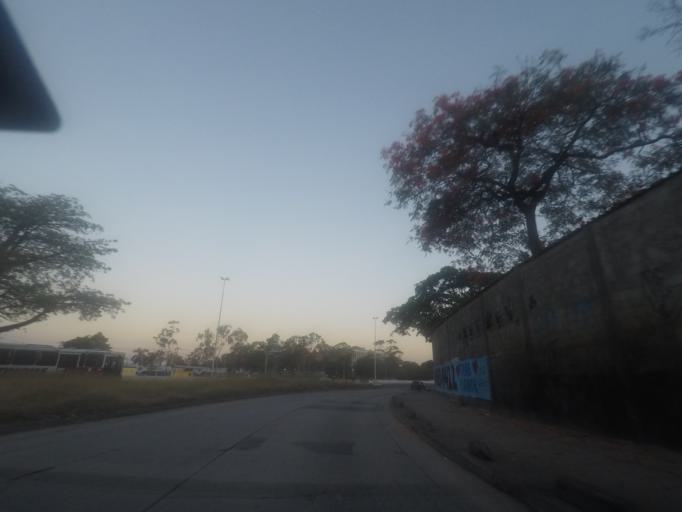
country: BR
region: Rio de Janeiro
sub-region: Duque De Caxias
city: Duque de Caxias
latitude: -22.8178
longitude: -43.2871
